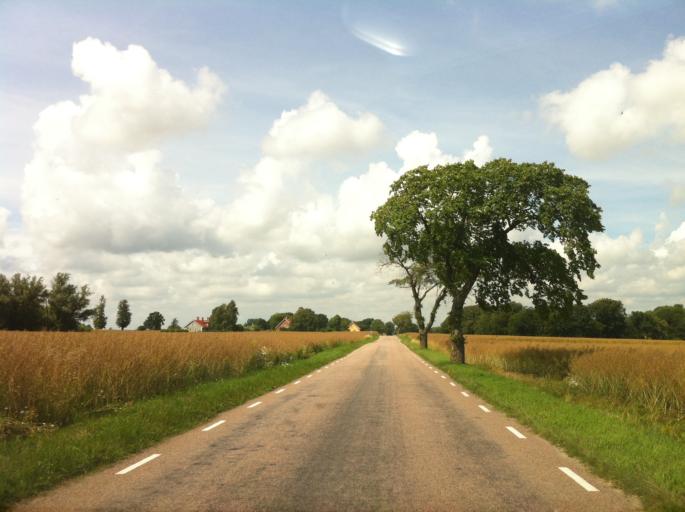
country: SE
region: Skane
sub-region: Trelleborgs Kommun
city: Anderslov
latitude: 55.4565
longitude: 13.4081
